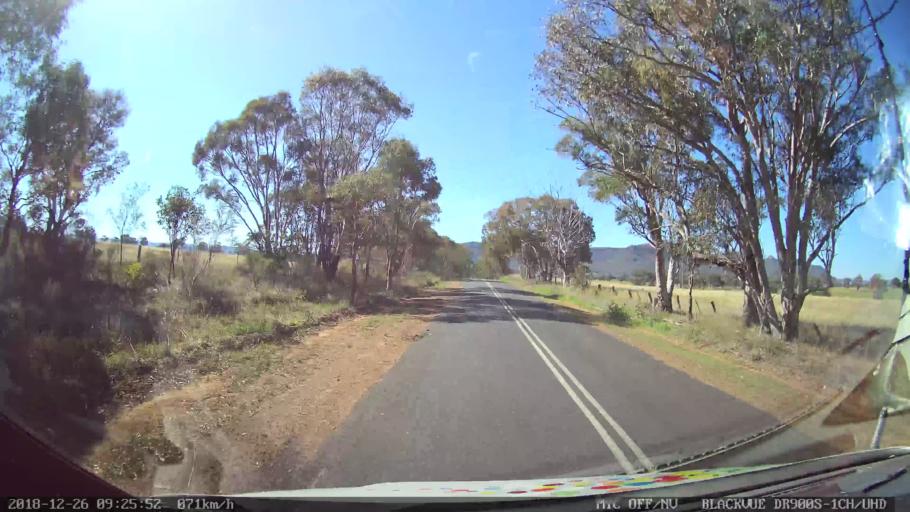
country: AU
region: New South Wales
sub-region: Mid-Western Regional
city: Kandos
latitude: -32.8241
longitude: 150.0056
